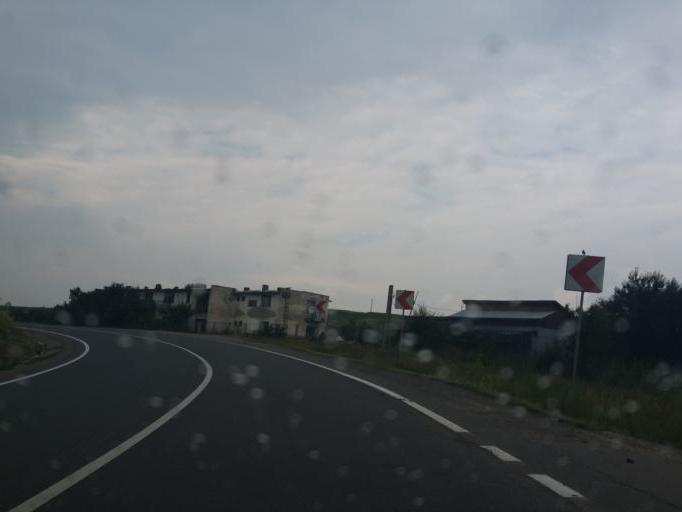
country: RO
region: Cluj
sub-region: Comuna Sanpaul
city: Sanpaul
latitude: 46.9178
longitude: 23.4232
